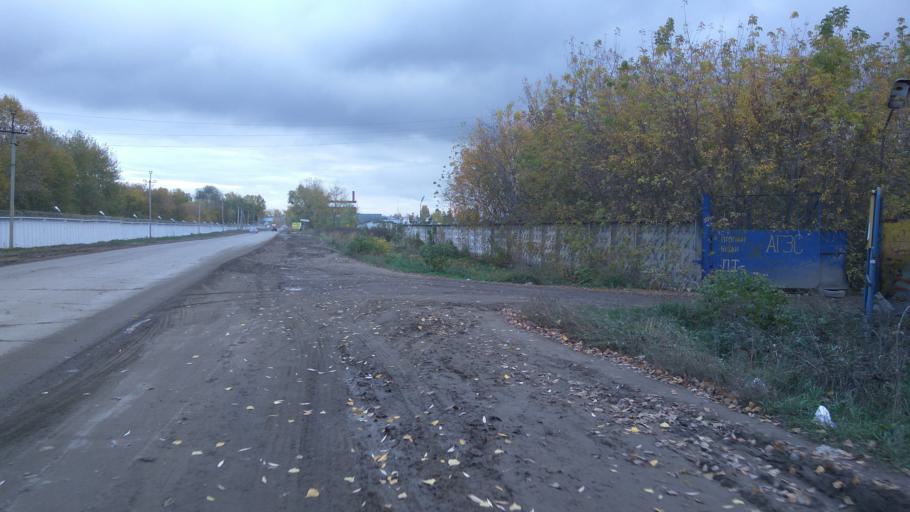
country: RU
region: Tatarstan
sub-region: Gorod Kazan'
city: Kazan
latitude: 55.7338
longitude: 49.1022
